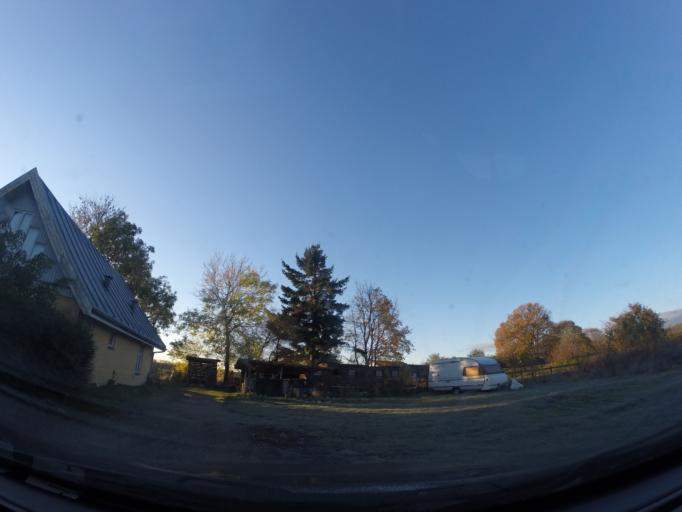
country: DK
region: Capital Region
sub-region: Hoje-Taastrup Kommune
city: Flong
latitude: 55.6666
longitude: 12.2382
